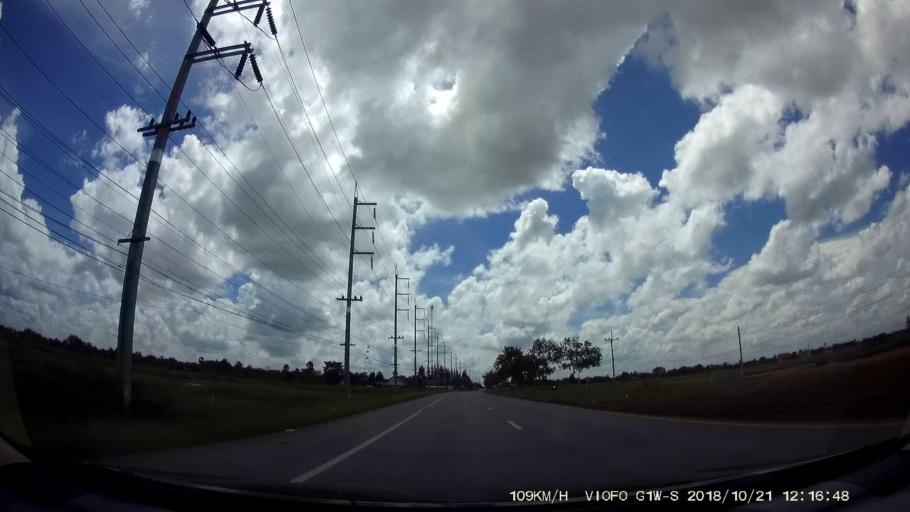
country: TH
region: Nakhon Ratchasima
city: Dan Khun Thot
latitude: 15.3420
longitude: 101.8241
